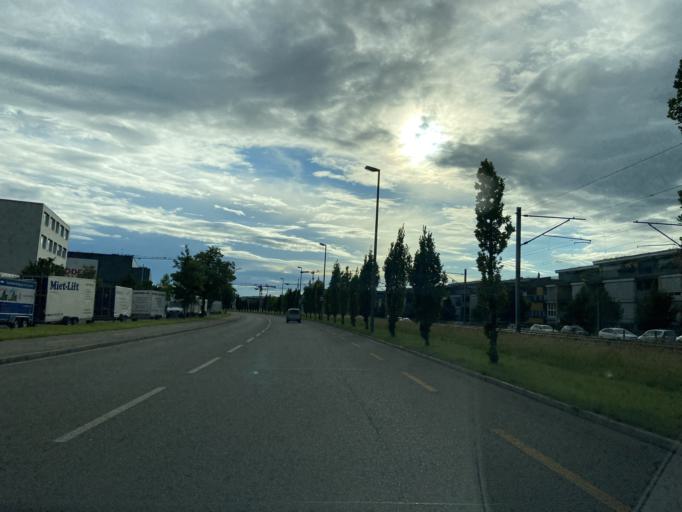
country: CH
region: Zurich
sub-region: Bezirk Winterthur
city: Oberwinterthur (Kreis 2) / Hegi
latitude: 47.5026
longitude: 8.7772
